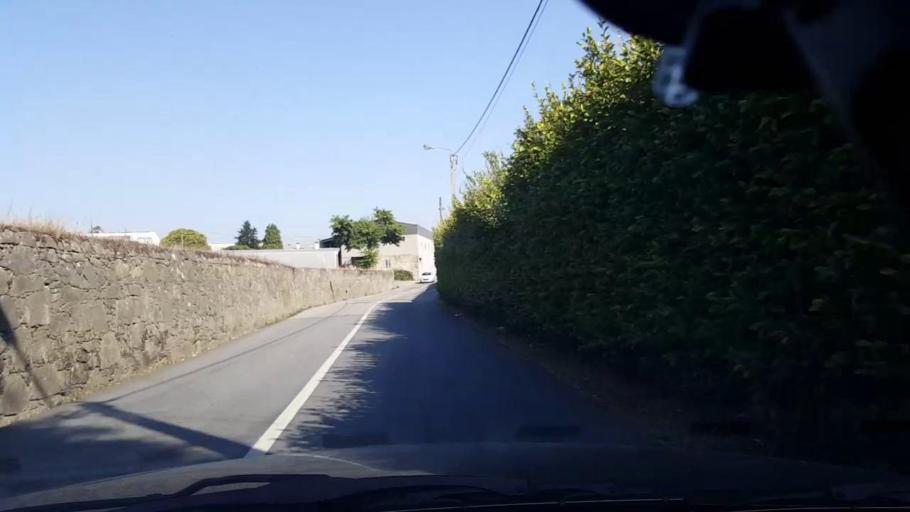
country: PT
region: Porto
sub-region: Vila do Conde
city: Arvore
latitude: 41.3366
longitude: -8.6823
